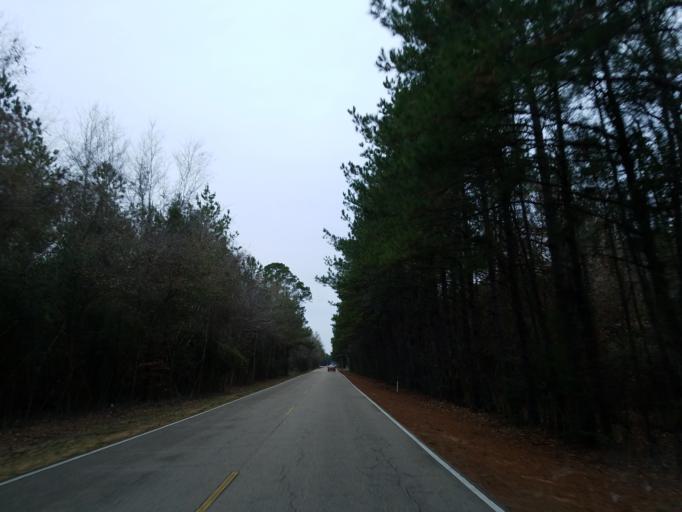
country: US
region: Mississippi
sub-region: Forrest County
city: Hattiesburg
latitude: 31.2607
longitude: -89.2369
